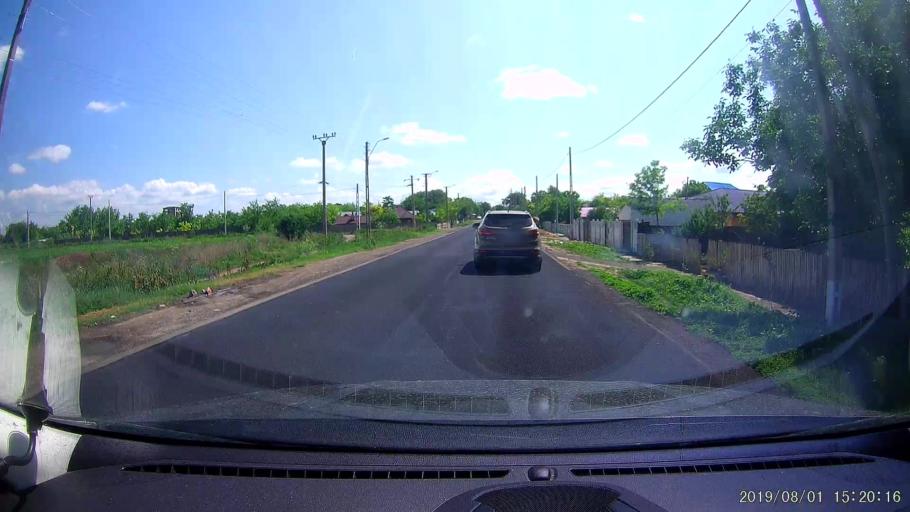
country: RO
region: Braila
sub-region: Comuna Tufesti
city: Tufesti
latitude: 45.0807
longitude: 27.8079
